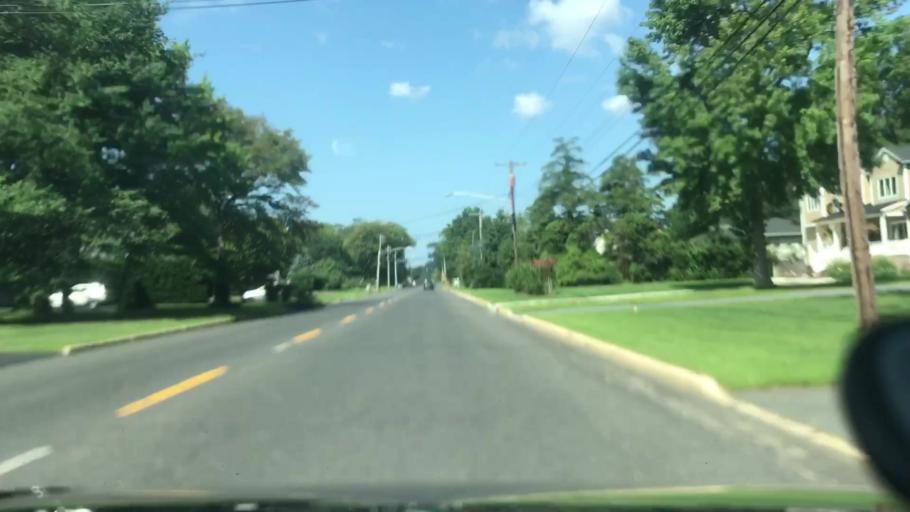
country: US
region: New Jersey
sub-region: Monmouth County
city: Oceanport
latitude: 40.3218
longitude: -74.0081
